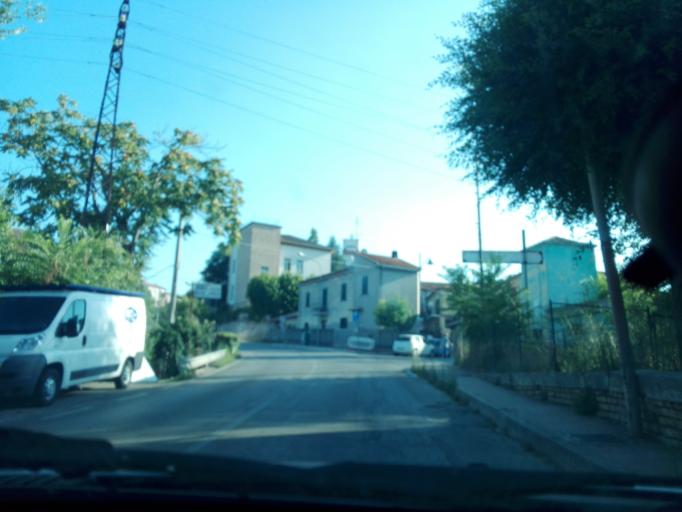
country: IT
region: Abruzzo
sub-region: Provincia di Pescara
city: Cappelle sul Tavo
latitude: 42.4667
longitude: 14.1040
